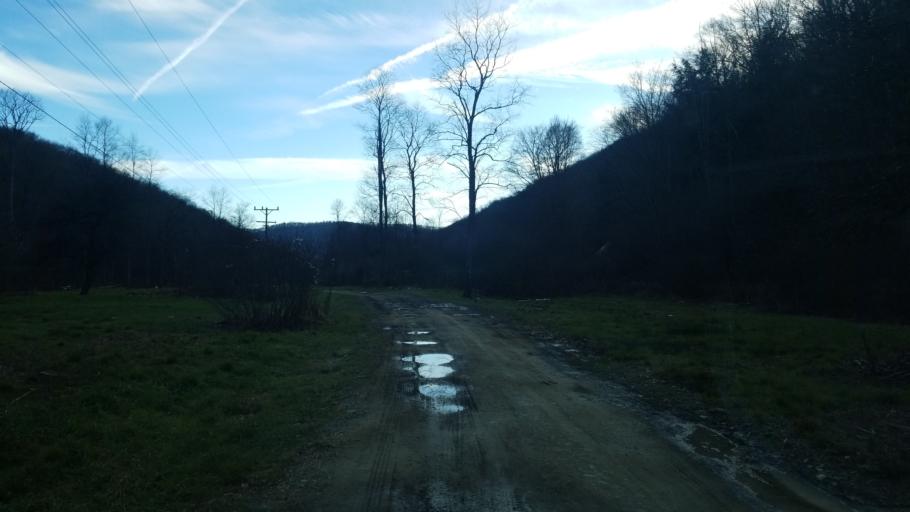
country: US
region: Pennsylvania
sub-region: Potter County
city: Coudersport
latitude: 41.6510
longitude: -78.0863
